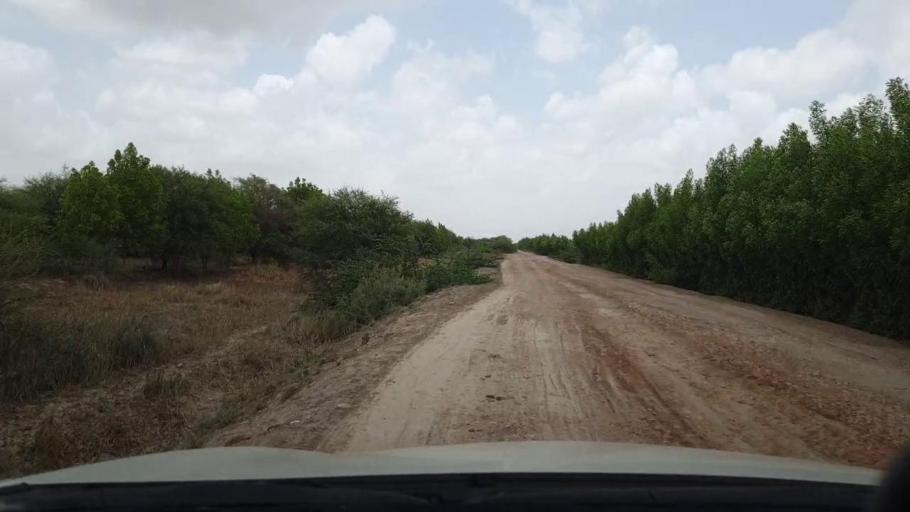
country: PK
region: Sindh
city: Kadhan
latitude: 24.3604
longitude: 68.9566
